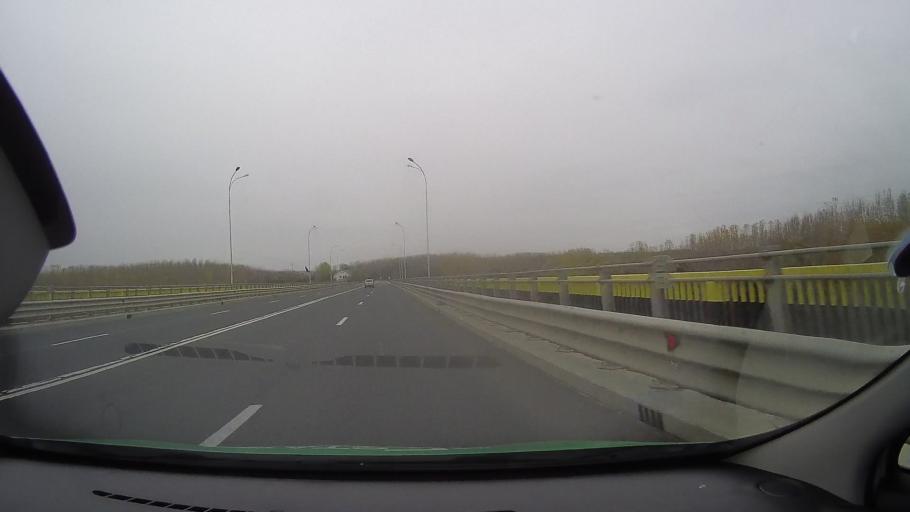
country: RO
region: Ialomita
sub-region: Comuna Giurgeni
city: Giurgeni
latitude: 44.7553
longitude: 27.8697
